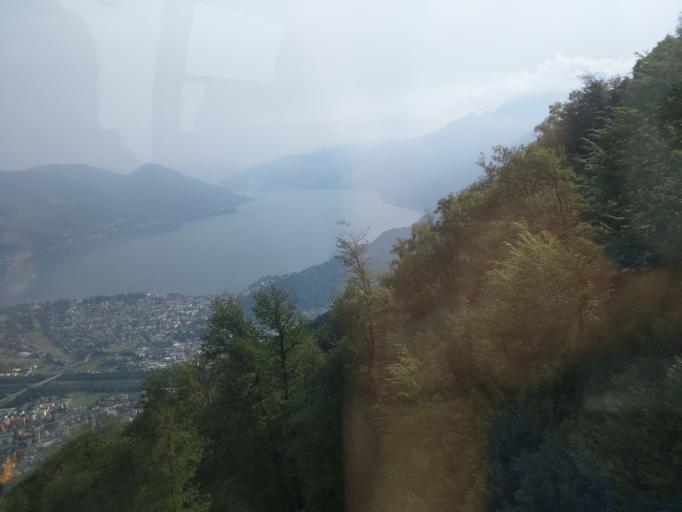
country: CH
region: Ticino
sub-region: Locarno District
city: Locarno
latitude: 46.1903
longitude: 8.7822
